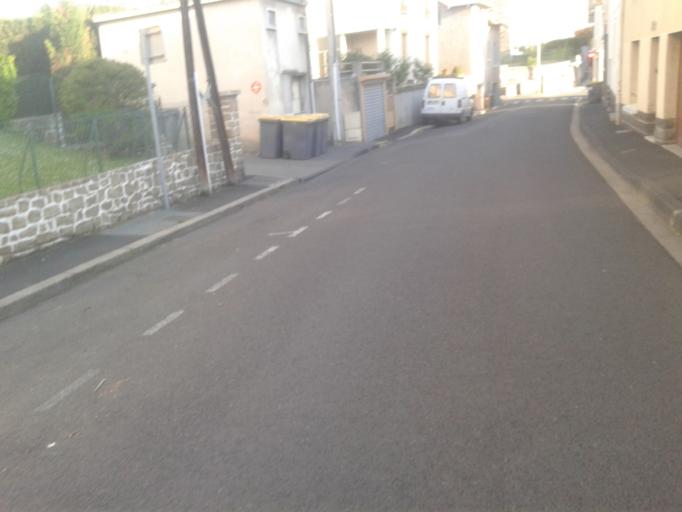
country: FR
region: Auvergne
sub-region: Departement du Puy-de-Dome
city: Chamalieres
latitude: 45.7676
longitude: 3.0701
